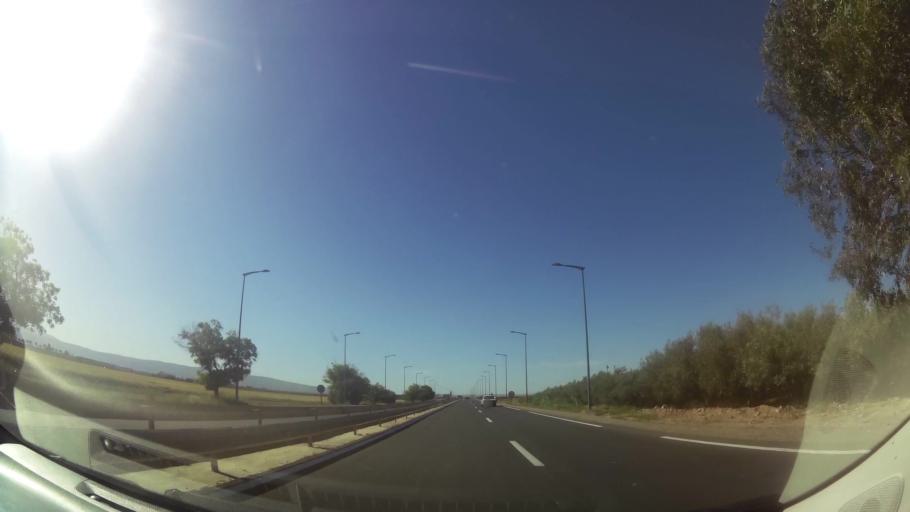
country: MA
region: Oriental
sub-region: Oujda-Angad
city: Oujda
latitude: 34.8014
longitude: -1.9562
